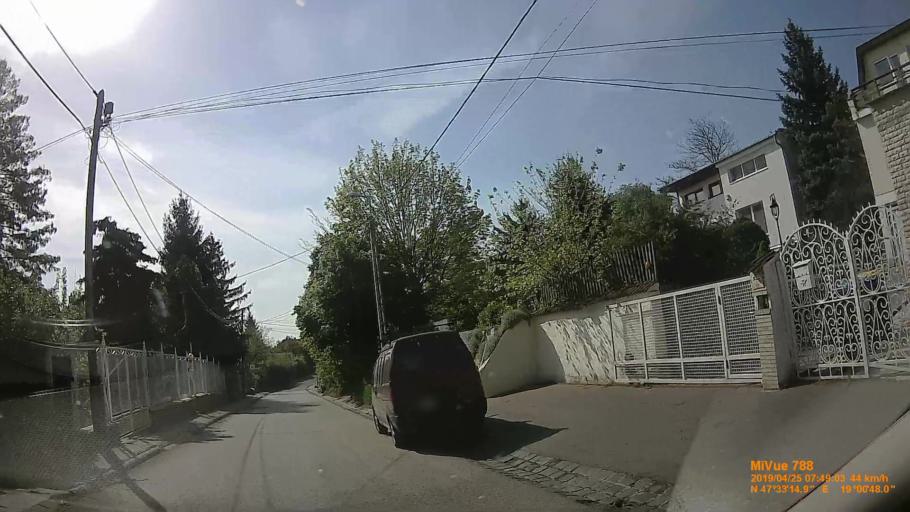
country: HU
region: Budapest
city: Budapest III. keruelet
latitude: 47.5541
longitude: 19.0134
